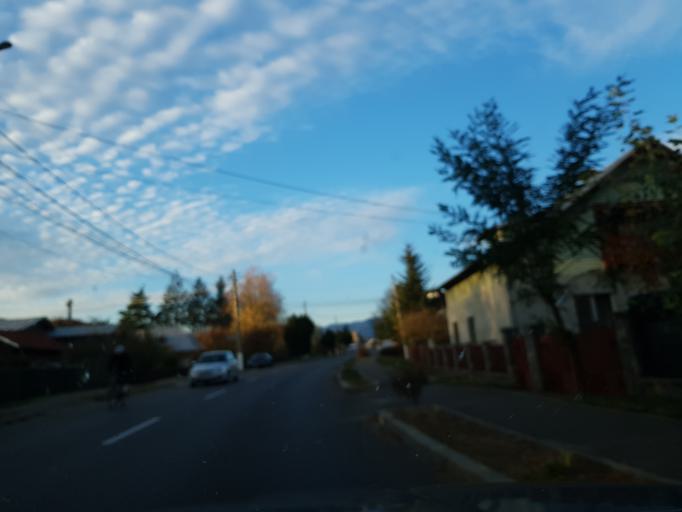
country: RO
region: Prahova
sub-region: Oras Breaza
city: Breaza de Sus
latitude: 45.1933
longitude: 25.6574
